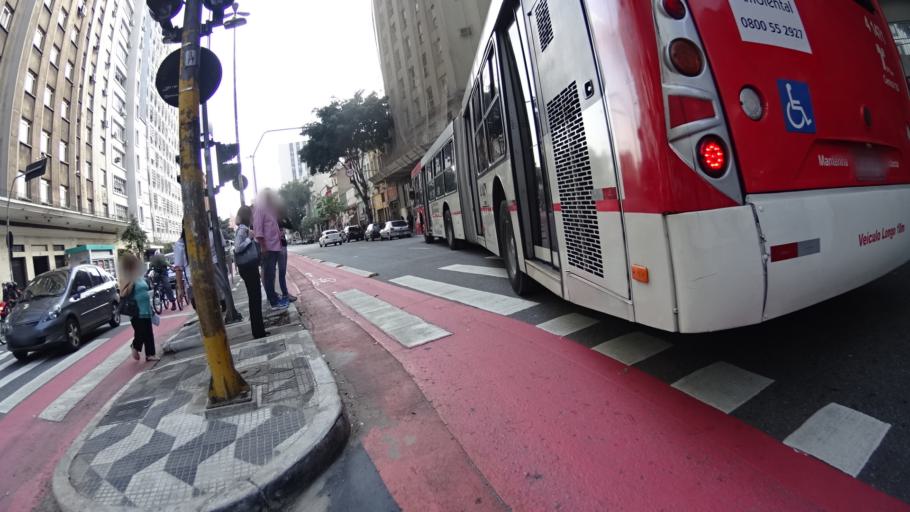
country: BR
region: Sao Paulo
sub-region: Sao Paulo
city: Sao Paulo
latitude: -23.5529
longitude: -46.6347
